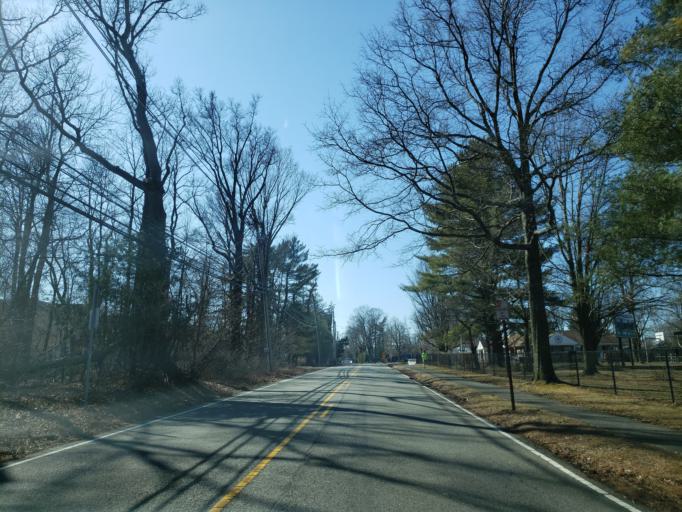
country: US
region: New Jersey
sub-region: Essex County
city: Short Hills
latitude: 40.7457
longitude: -74.3350
